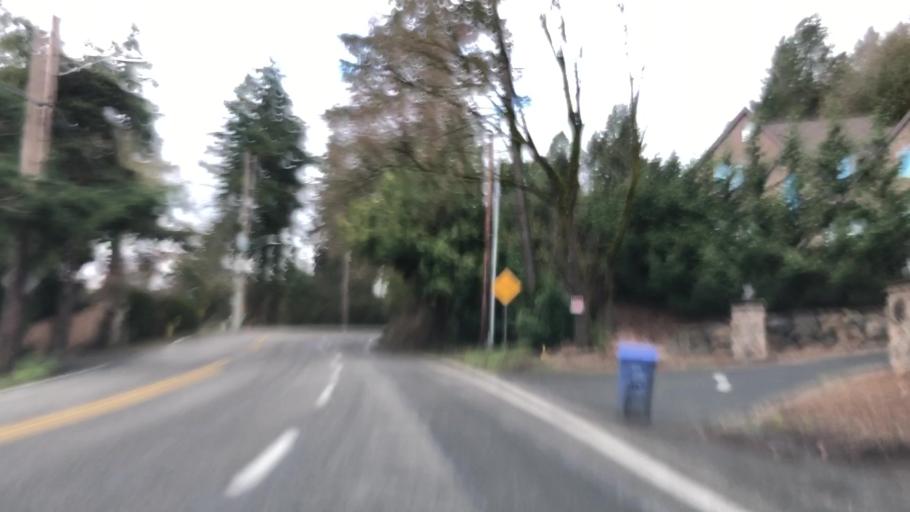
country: US
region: Oregon
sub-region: Washington County
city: West Slope
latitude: 45.4992
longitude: -122.7401
